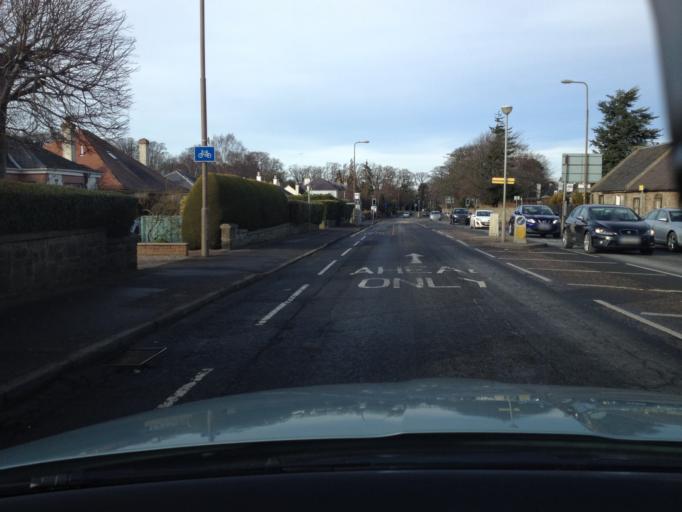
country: GB
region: Scotland
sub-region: Midlothian
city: Loanhead
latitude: 55.9006
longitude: -3.1634
